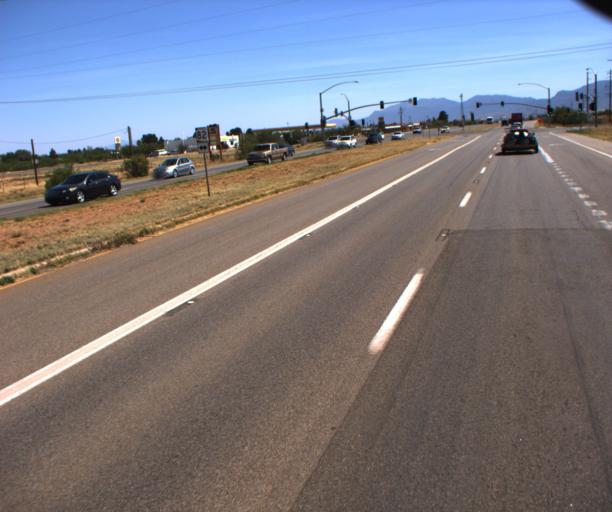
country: US
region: Arizona
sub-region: Cochise County
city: Huachuca City
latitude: 31.6940
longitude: -110.3504
